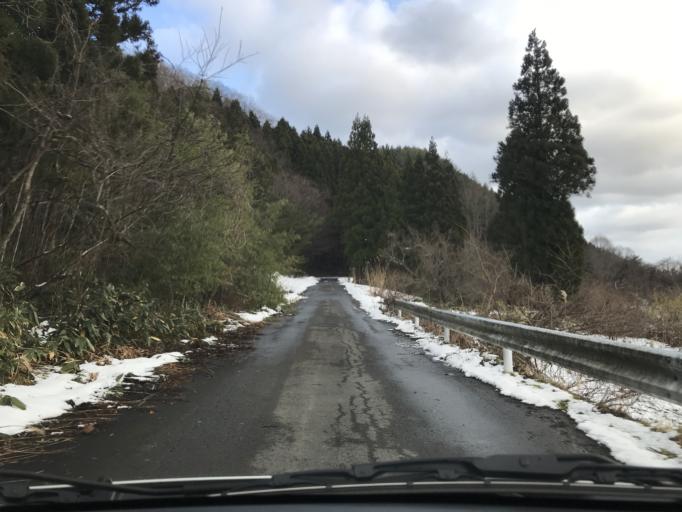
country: JP
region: Iwate
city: Ichinoseki
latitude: 39.0192
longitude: 140.9692
